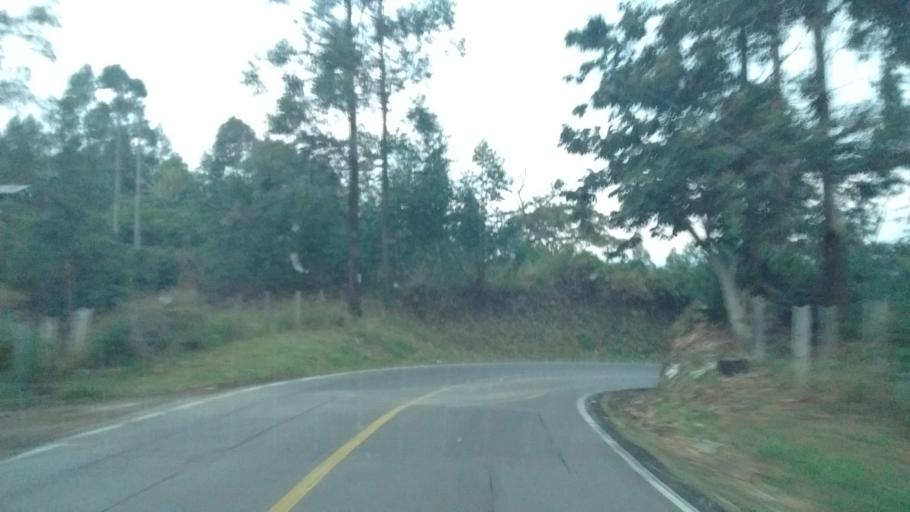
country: CO
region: Cauca
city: Popayan
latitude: 2.3676
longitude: -76.6873
